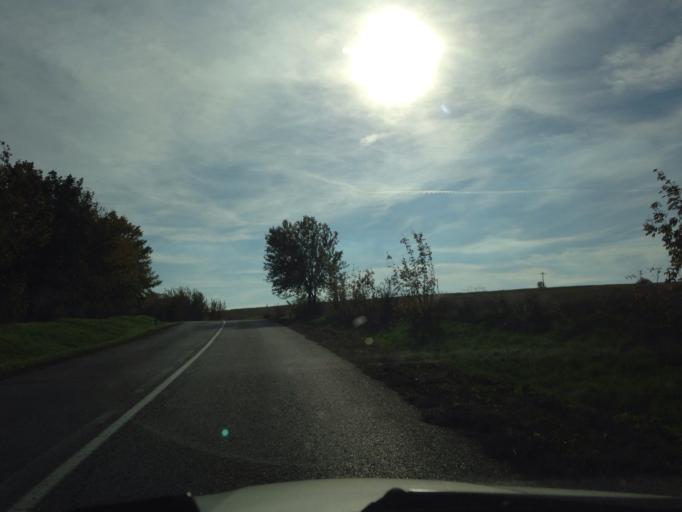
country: SK
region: Nitriansky
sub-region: Okres Komarno
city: Hurbanovo
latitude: 47.8785
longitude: 18.2867
